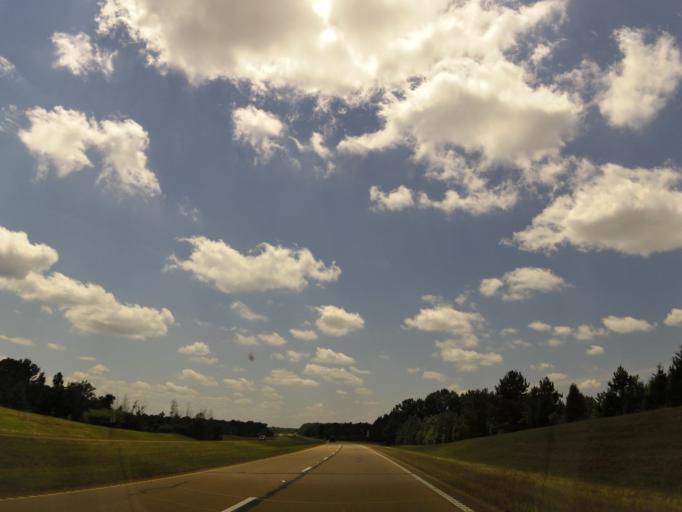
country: US
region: Mississippi
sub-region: Pontotoc County
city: Pontotoc
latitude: 34.2860
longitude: -89.0945
